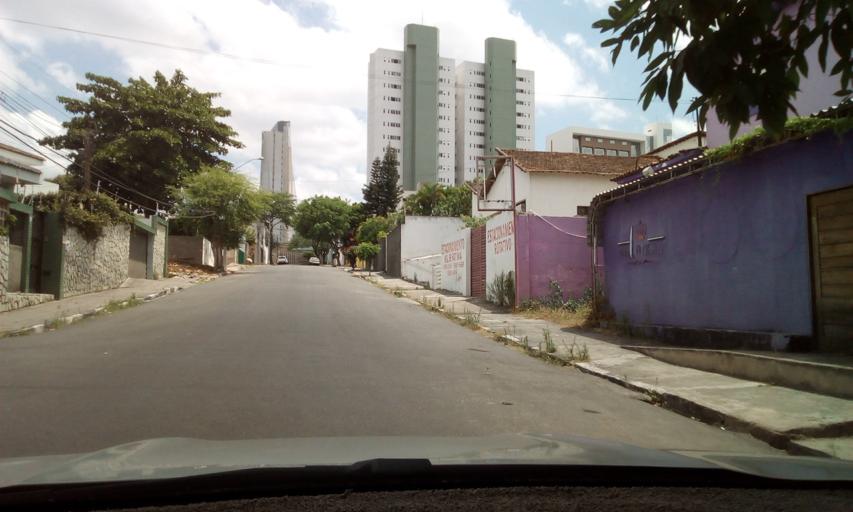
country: BR
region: Pernambuco
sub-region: Caruaru
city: Caruaru
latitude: -8.2785
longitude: -35.9699
